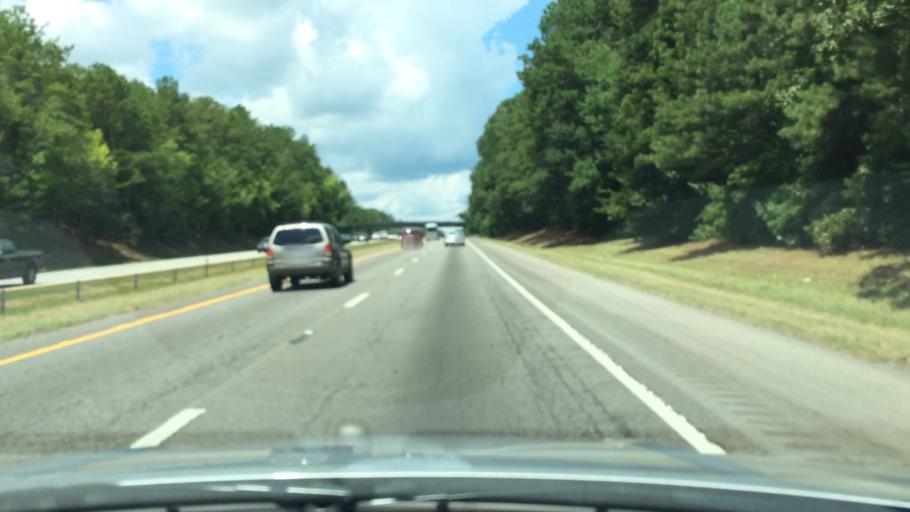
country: US
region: South Carolina
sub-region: Lexington County
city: Chapin
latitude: 34.1907
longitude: -81.3458
